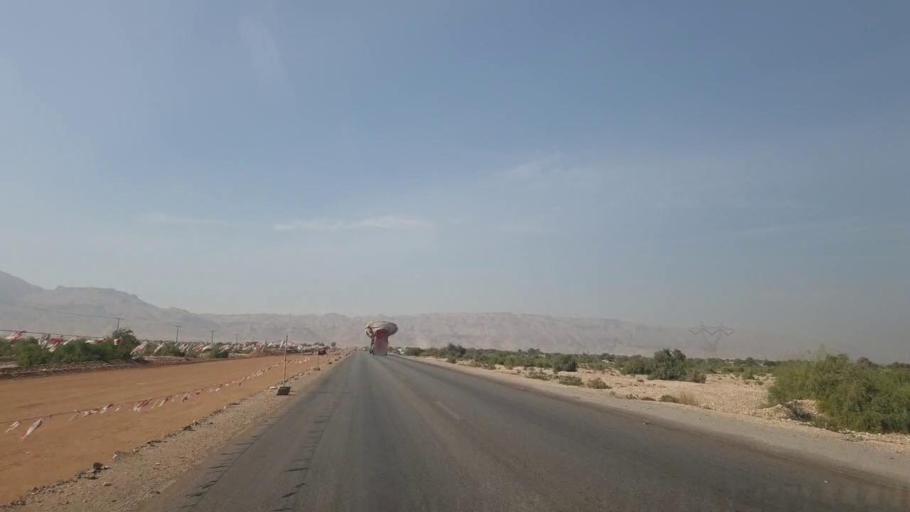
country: PK
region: Sindh
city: Sehwan
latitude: 26.2144
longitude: 67.9178
